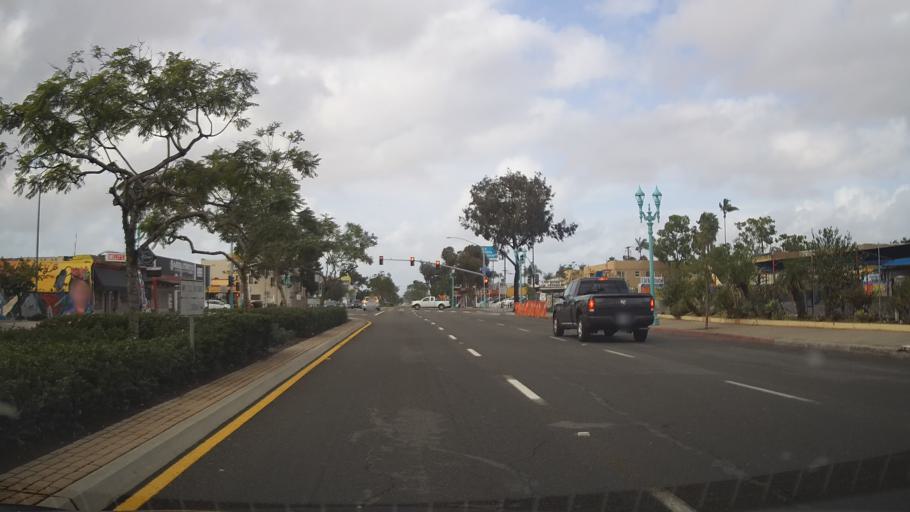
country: US
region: California
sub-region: San Diego County
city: San Diego
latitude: 32.7553
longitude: -117.1167
